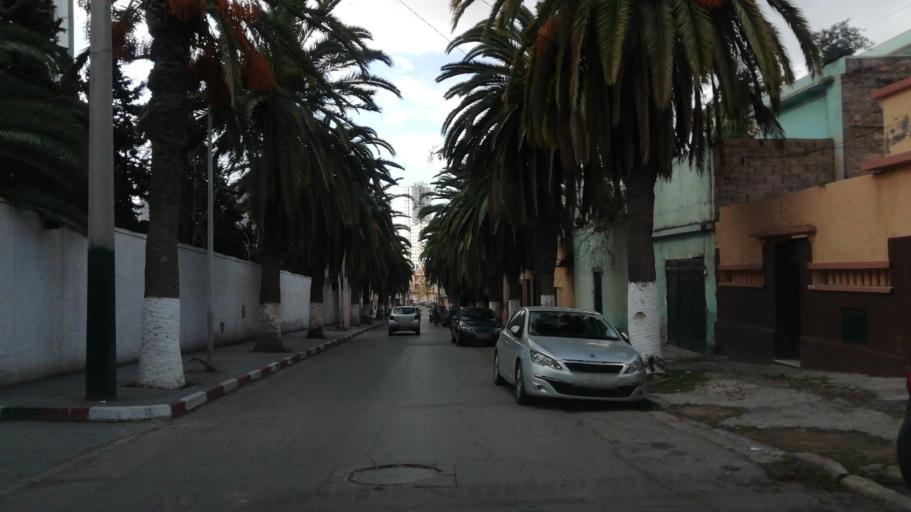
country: DZ
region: Oran
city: Oran
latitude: 35.7119
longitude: -0.6150
